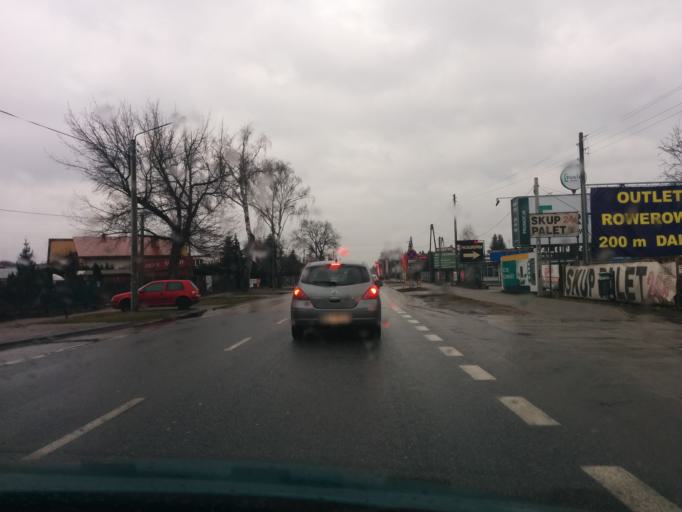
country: PL
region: Masovian Voivodeship
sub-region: Powiat legionowski
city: Jablonna
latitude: 52.3648
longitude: 20.9336
